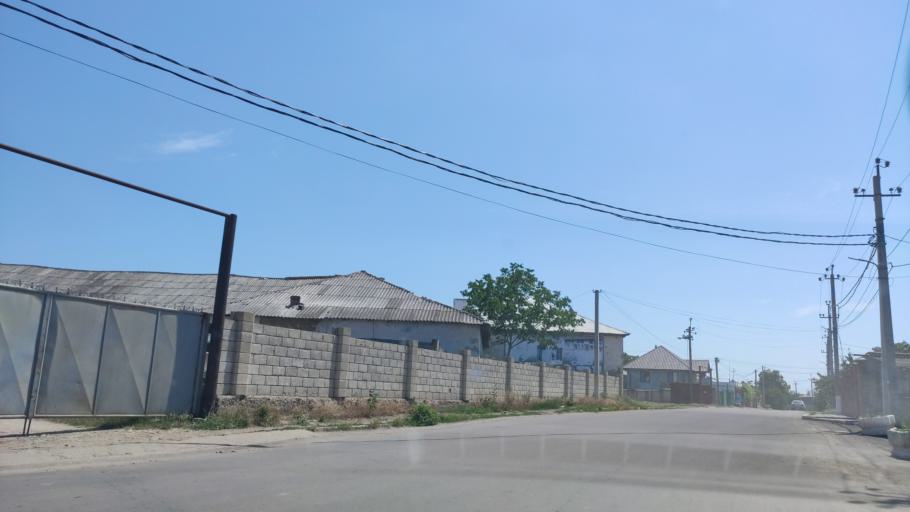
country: MD
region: Raionul Soroca
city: Soroca
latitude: 48.1513
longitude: 28.2767
